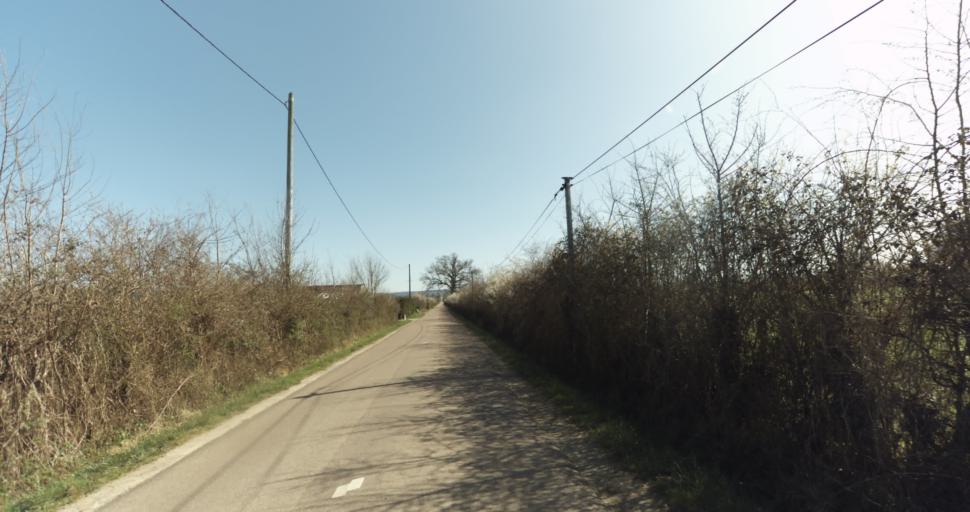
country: FR
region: Lower Normandy
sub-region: Departement du Calvados
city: Saint-Pierre-sur-Dives
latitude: 48.9536
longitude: 0.0105
